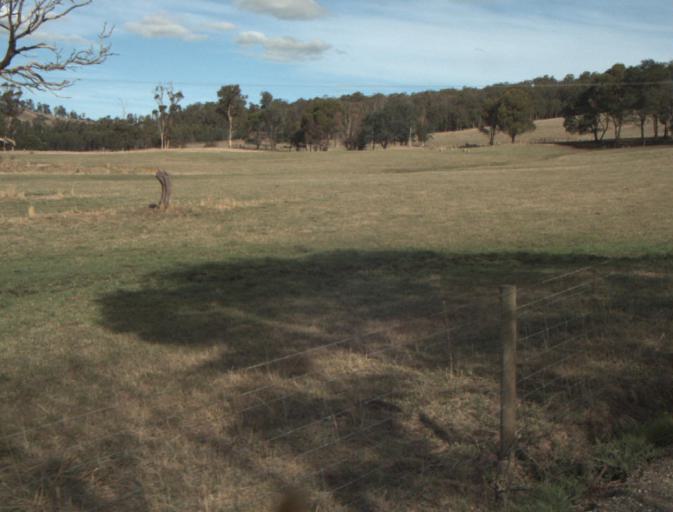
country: AU
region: Tasmania
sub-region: Launceston
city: Mayfield
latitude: -41.2200
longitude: 147.1583
